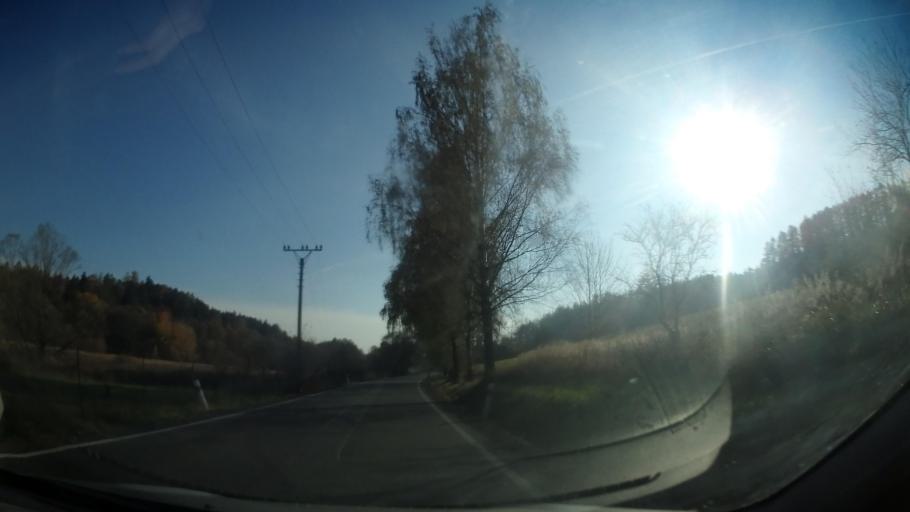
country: CZ
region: Central Bohemia
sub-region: Okres Praha-Vychod
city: Mnichovice
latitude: 49.9246
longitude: 14.7182
